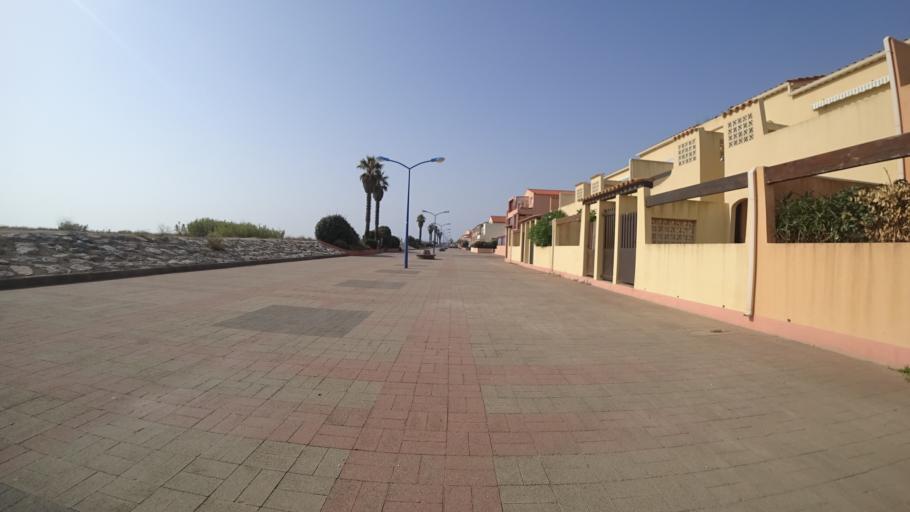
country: FR
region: Languedoc-Roussillon
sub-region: Departement des Pyrenees-Orientales
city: Sainte-Marie-Plage
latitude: 42.7368
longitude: 3.0367
